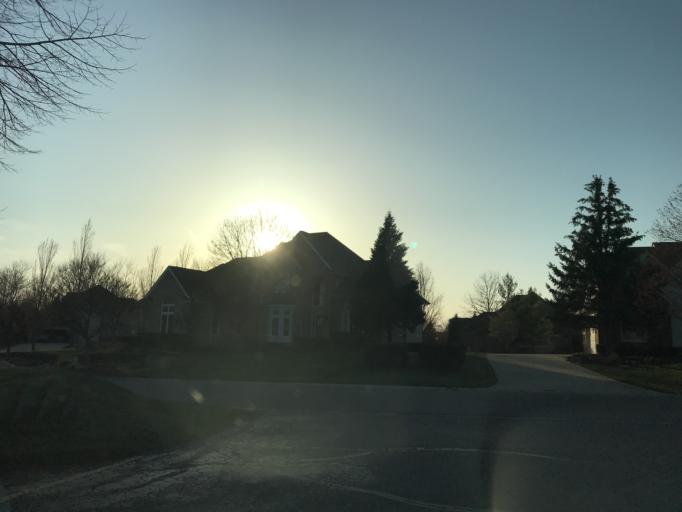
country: US
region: Michigan
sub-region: Oakland County
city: South Lyon
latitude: 42.4557
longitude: -83.5800
